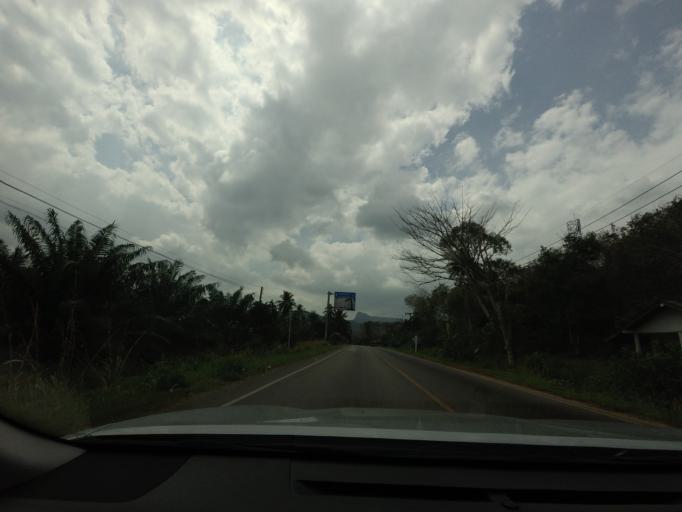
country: TH
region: Phangnga
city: Ban Ao Nang
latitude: 8.1208
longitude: 98.8026
